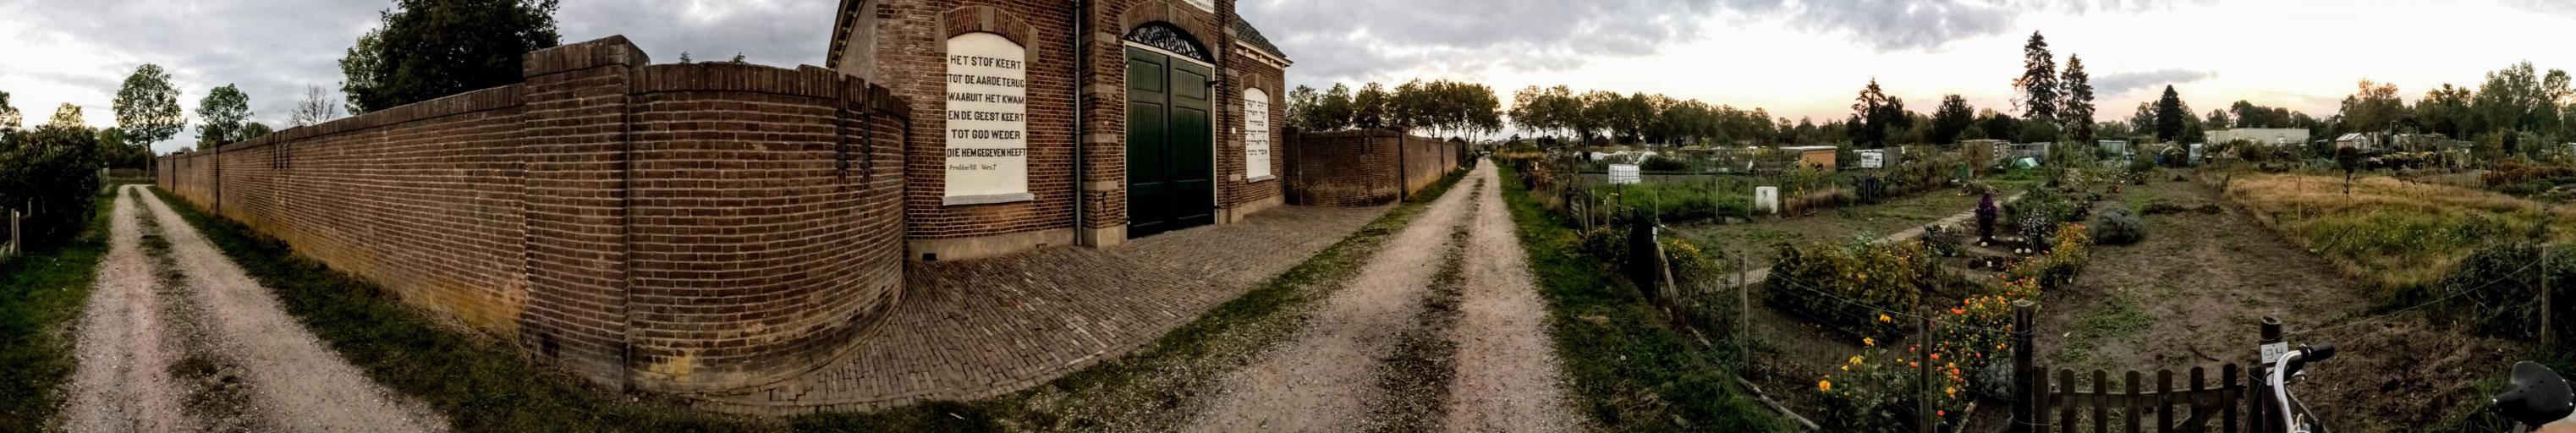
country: NL
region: Gelderland
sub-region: Gemeente Zutphen
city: Zutphen
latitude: 52.1294
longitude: 6.2054
